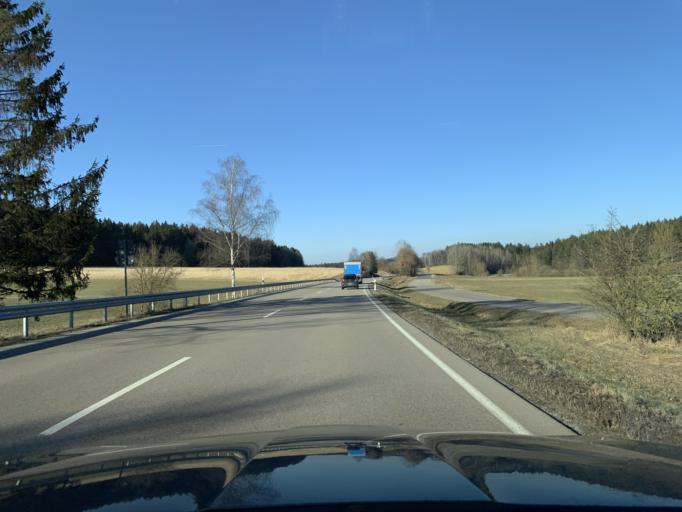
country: DE
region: Bavaria
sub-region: Upper Palatinate
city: Schonthal
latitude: 49.3139
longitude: 12.6311
